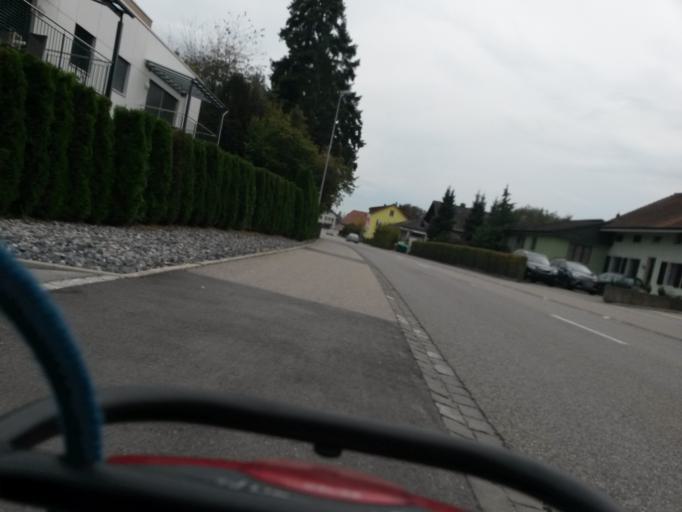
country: CH
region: Solothurn
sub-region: Bezirk Wasseramt
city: Biberist
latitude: 47.1856
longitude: 7.5570
